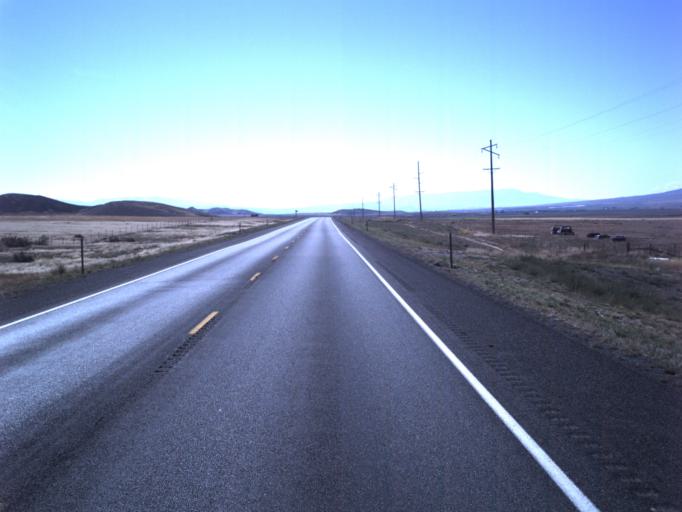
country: US
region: Utah
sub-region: Sanpete County
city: Gunnison
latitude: 39.2199
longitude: -111.8482
